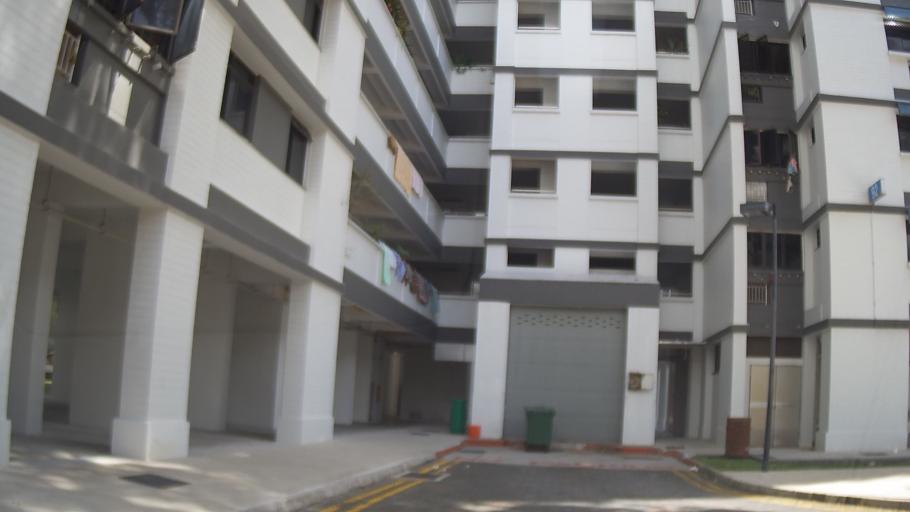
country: SG
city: Singapore
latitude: 1.3231
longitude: 103.8870
